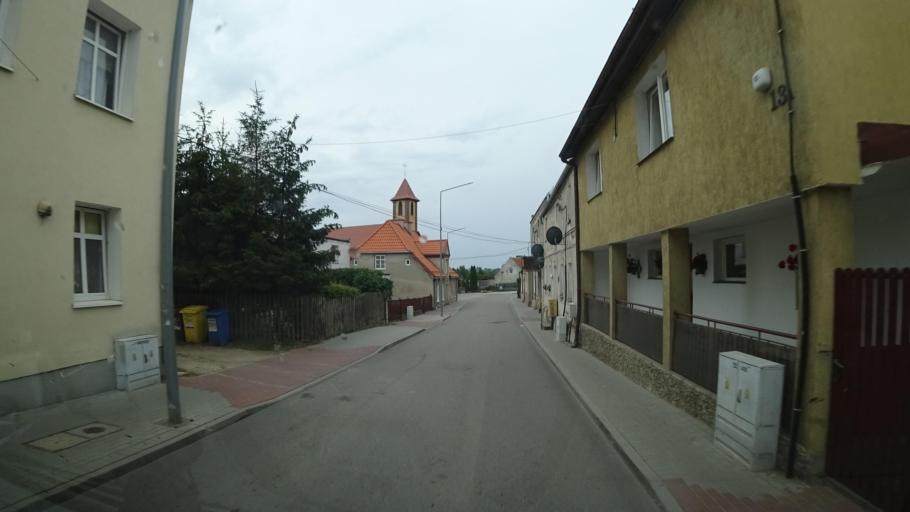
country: PL
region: Warmian-Masurian Voivodeship
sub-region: Powiat gizycki
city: Ryn
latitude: 53.9378
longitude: 21.5493
